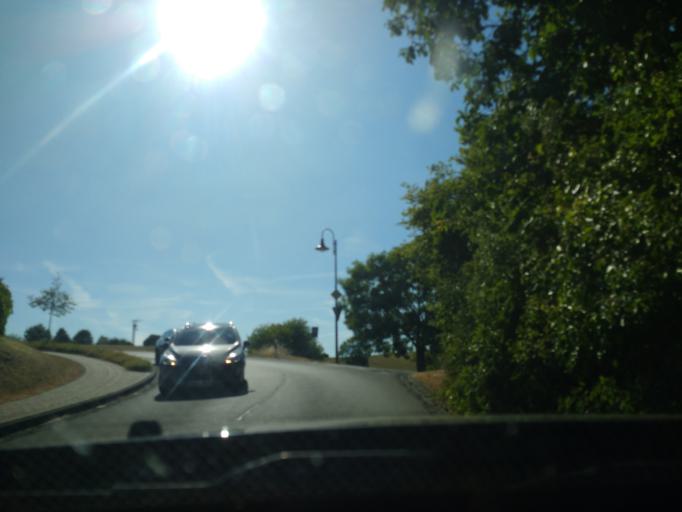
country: DE
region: Rheinland-Pfalz
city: Udersdorf
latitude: 50.1531
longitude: 6.8003
